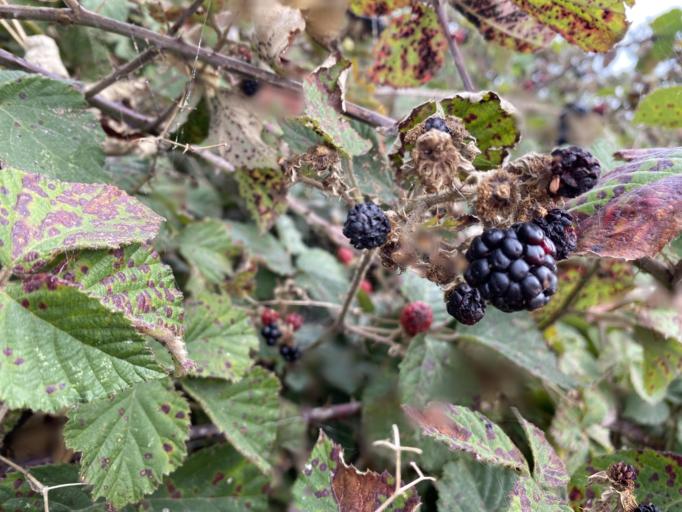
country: DK
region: Zealand
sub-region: Naestved Kommune
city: Naestved
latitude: 55.0650
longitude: 11.7121
